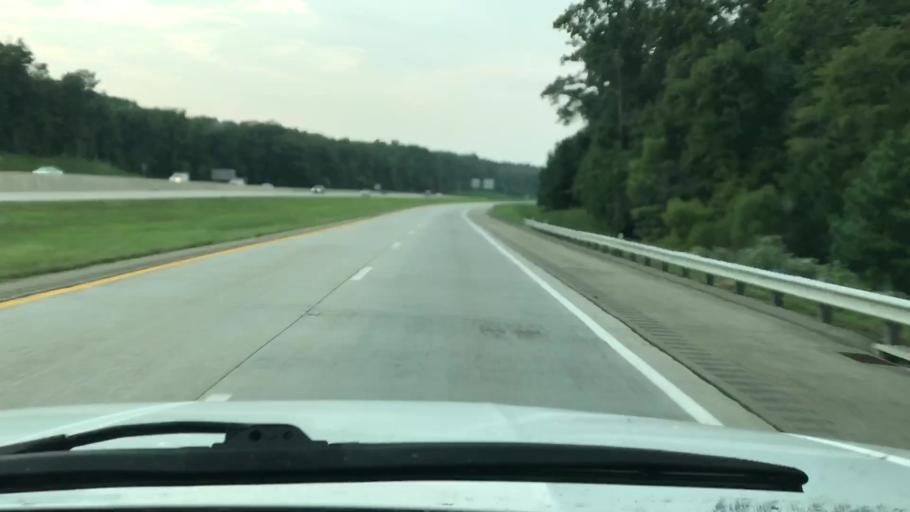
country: US
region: Virginia
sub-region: Chesterfield County
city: Brandermill
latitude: 37.5220
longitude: -77.6922
